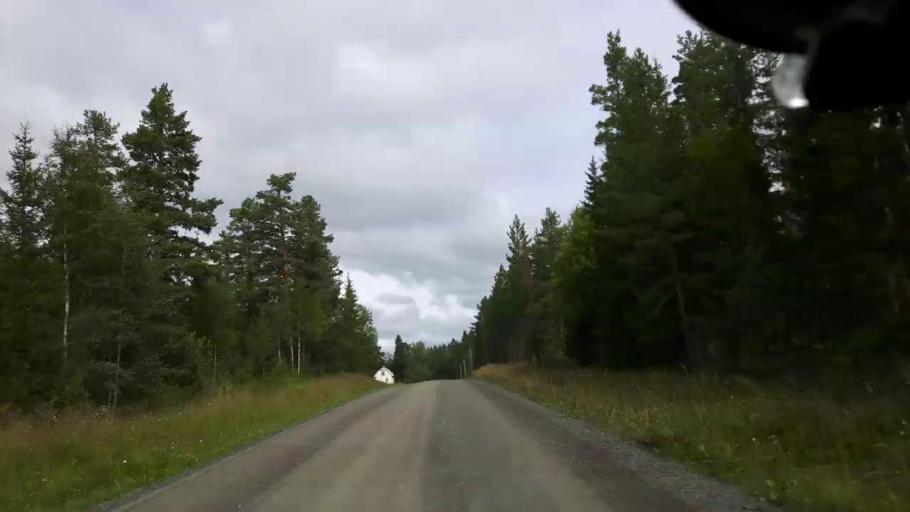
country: SE
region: Jaemtland
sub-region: Krokoms Kommun
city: Valla
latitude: 63.4038
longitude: 14.0939
